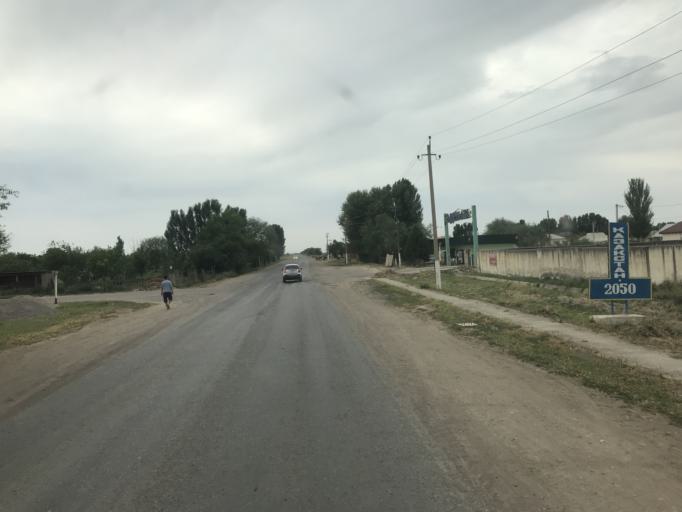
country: KZ
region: Ongtustik Qazaqstan
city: Asykata
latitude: 40.9056
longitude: 68.3543
